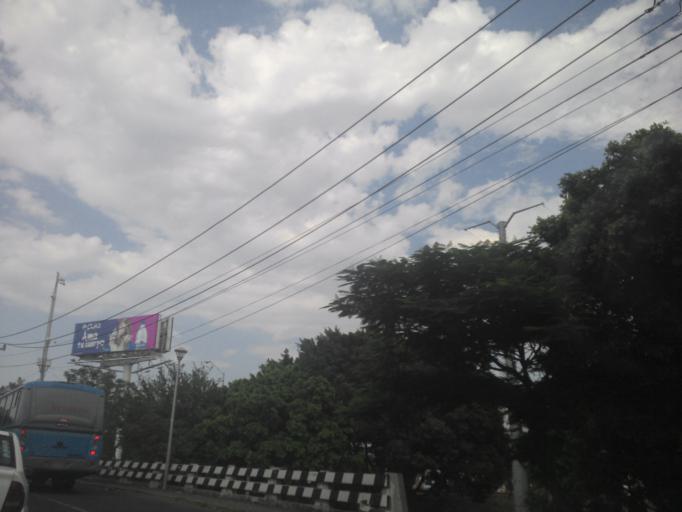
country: MX
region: Jalisco
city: Guadalajara
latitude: 20.6590
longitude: -103.3835
